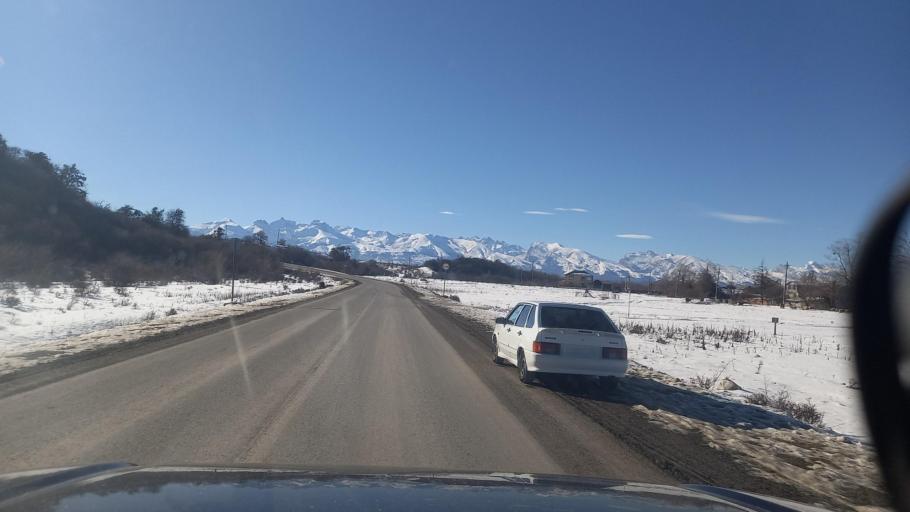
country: RU
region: North Ossetia
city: Chikola
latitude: 43.2232
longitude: 43.9280
